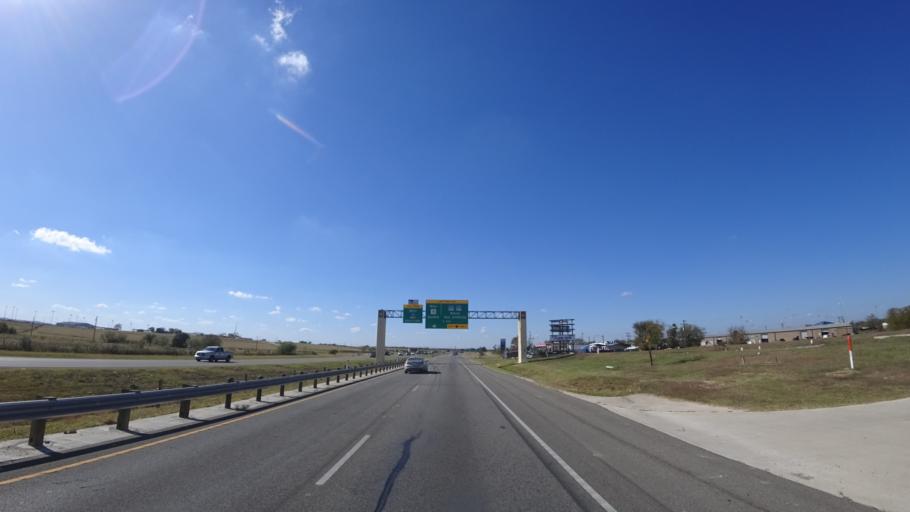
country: US
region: Texas
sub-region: Travis County
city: Garfield
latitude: 30.1870
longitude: -97.6044
